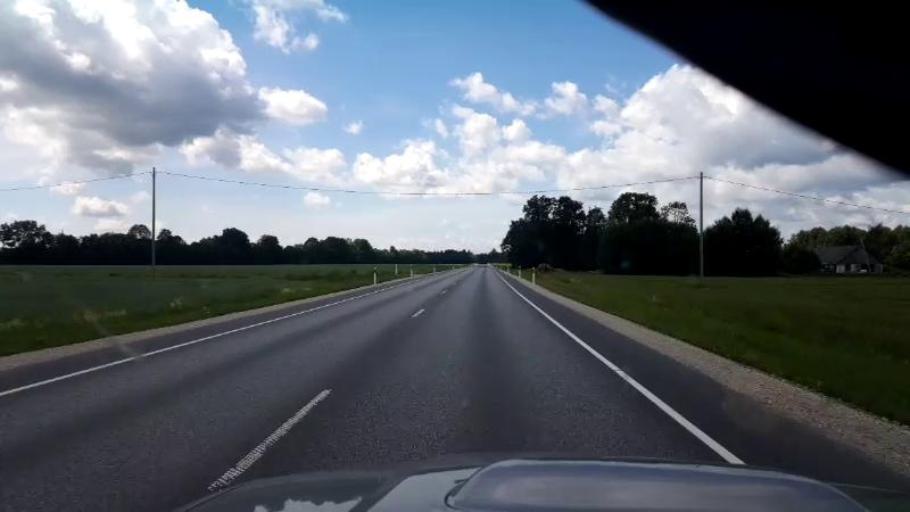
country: EE
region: Jaervamaa
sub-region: Jaerva-Jaani vald
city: Jarva-Jaani
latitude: 59.0138
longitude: 25.6983
